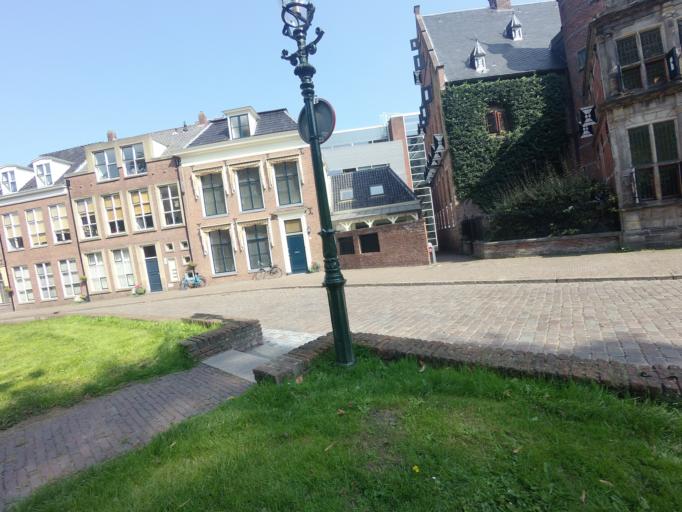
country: NL
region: Groningen
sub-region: Gemeente Groningen
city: Groningen
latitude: 53.2201
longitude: 6.5696
